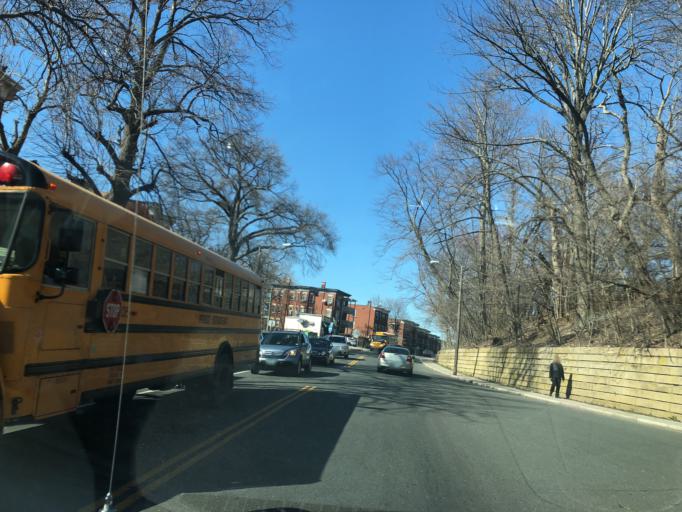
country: US
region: Connecticut
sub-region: Hartford County
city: Hartford
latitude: 41.7534
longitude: -72.6933
